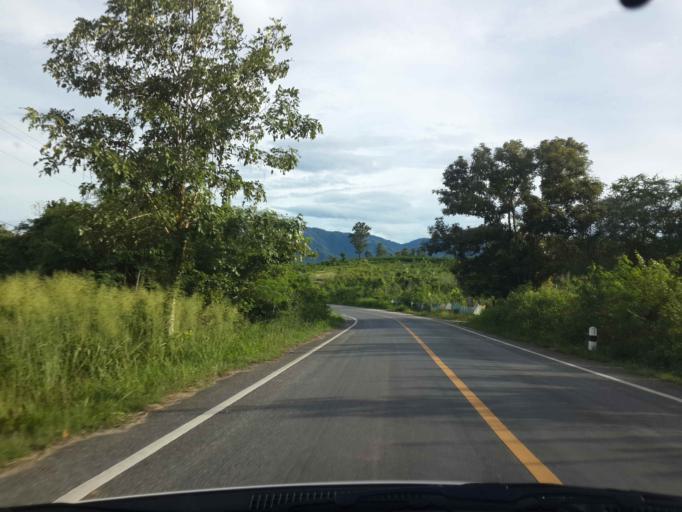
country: TH
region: Kanchanaburi
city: Dan Makham Tia
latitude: 13.8238
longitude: 99.1672
